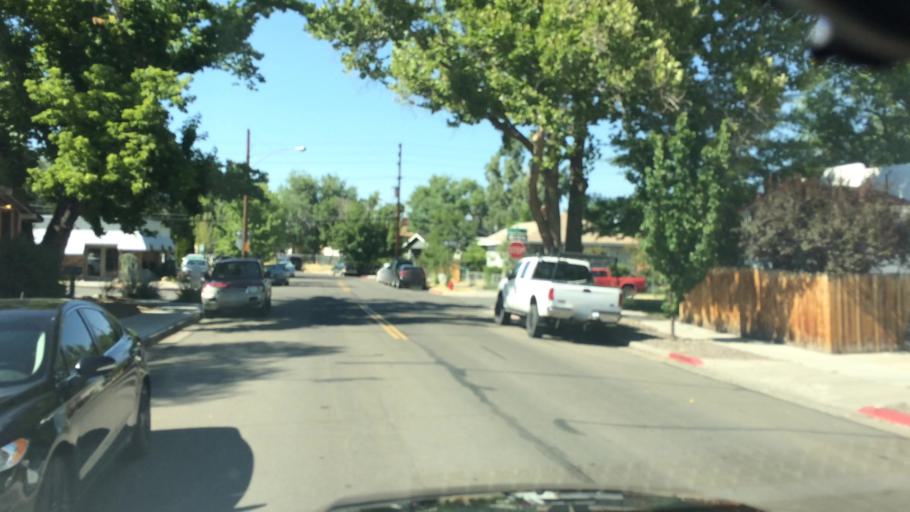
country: US
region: Nevada
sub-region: Washoe County
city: Reno
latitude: 39.5121
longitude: -119.8081
